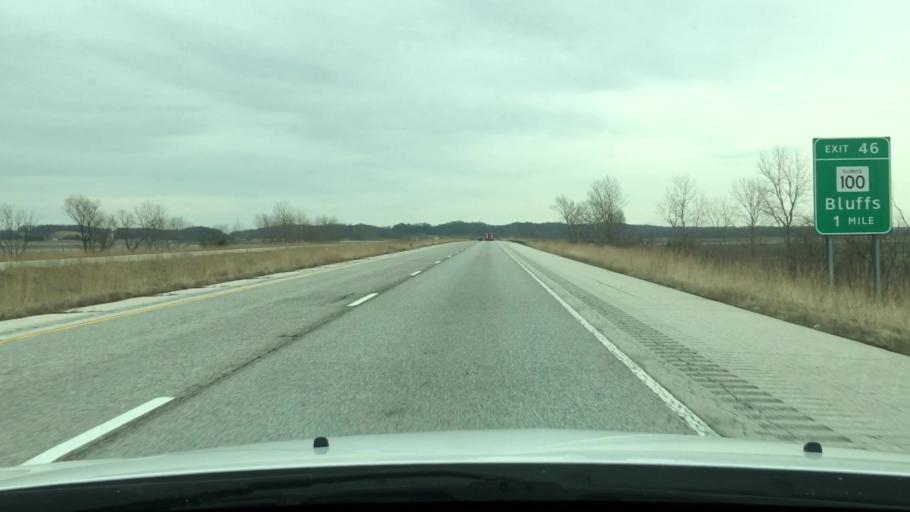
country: US
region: Illinois
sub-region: Pike County
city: Griggsville
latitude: 39.6889
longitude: -90.5996
